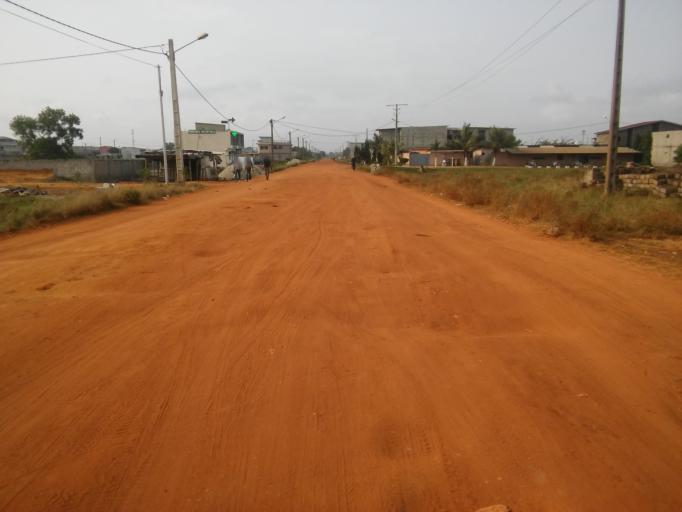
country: CI
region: Sud-Comoe
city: Grand-Bassam
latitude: 5.2119
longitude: -3.7650
